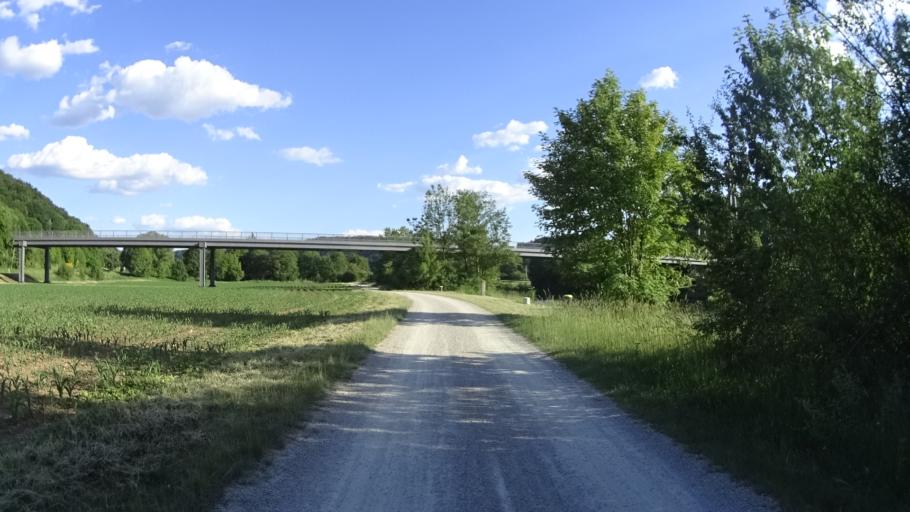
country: DE
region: Bavaria
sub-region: Upper Palatinate
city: Dietfurt
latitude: 48.9945
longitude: 11.6315
